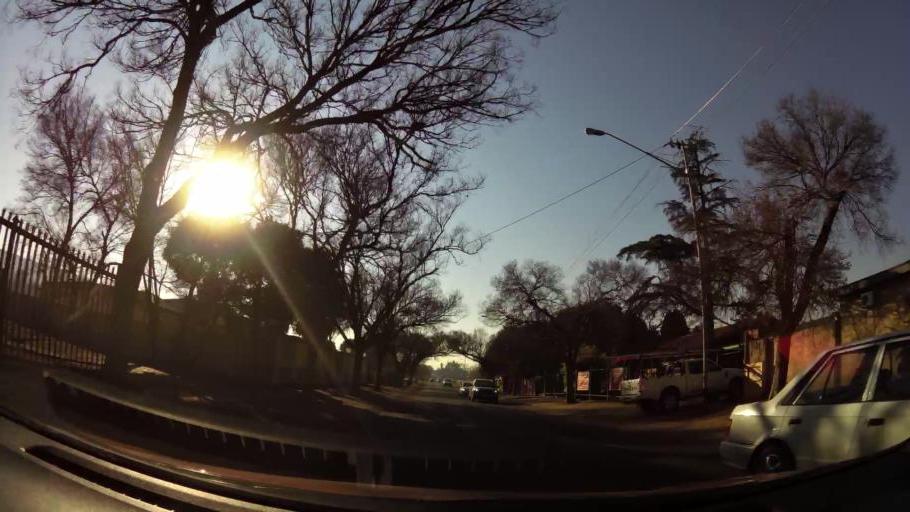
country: ZA
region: Gauteng
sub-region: City of Tshwane Metropolitan Municipality
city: Pretoria
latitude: -25.7057
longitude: 28.1966
